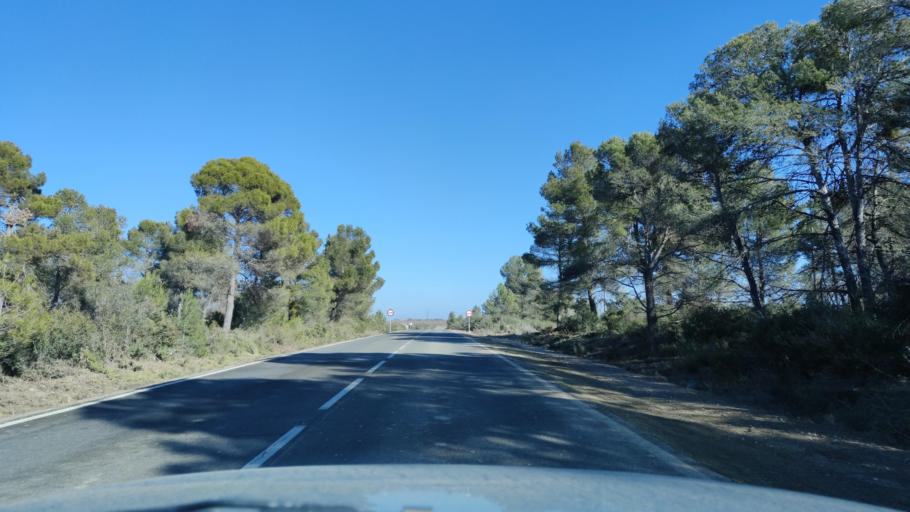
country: ES
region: Catalonia
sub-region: Provincia de Lleida
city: Maials
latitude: 41.3434
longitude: 0.4667
